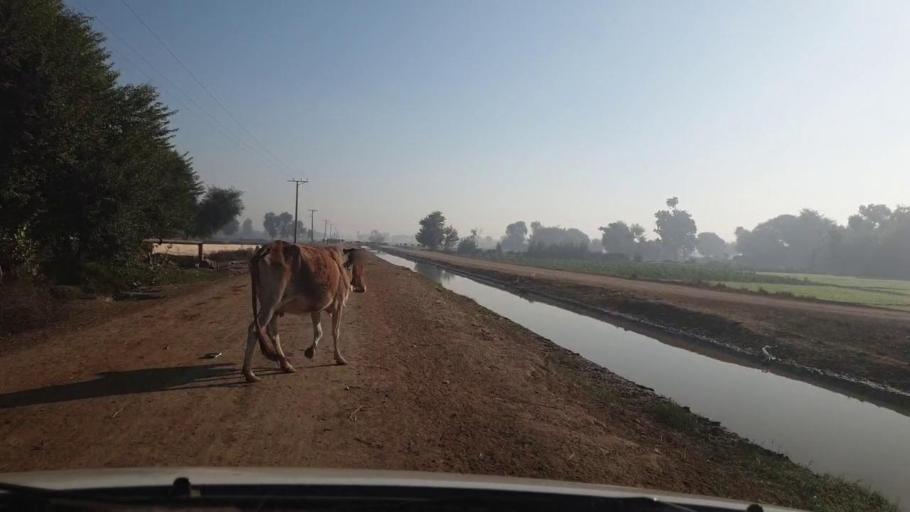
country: PK
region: Sindh
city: Dadu
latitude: 26.6825
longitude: 67.7870
